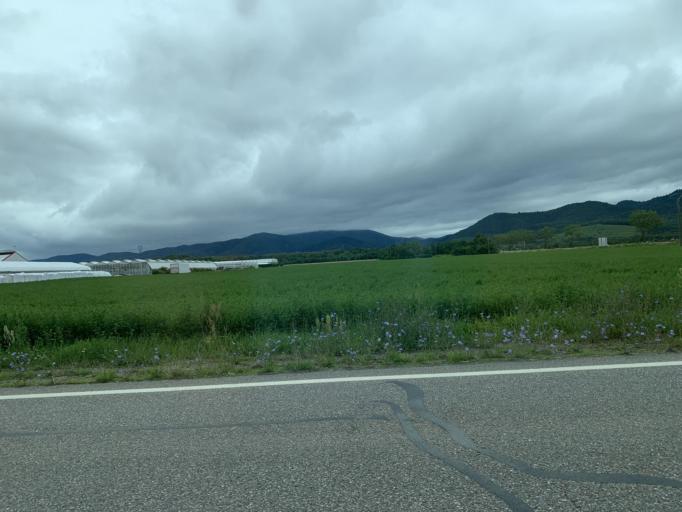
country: FR
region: Alsace
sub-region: Departement du Haut-Rhin
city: Cernay
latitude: 47.7942
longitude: 7.1578
